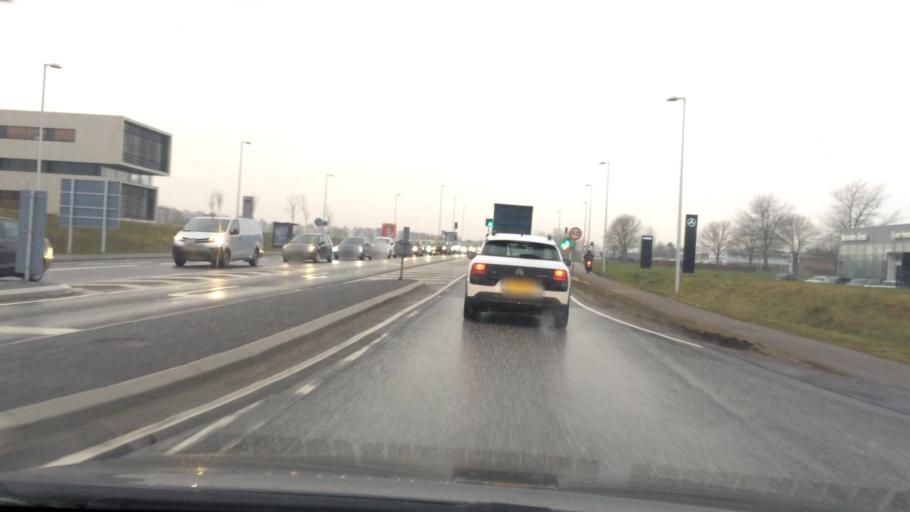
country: DK
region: Central Jutland
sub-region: Horsens Kommune
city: Horsens
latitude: 55.8315
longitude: 9.8046
